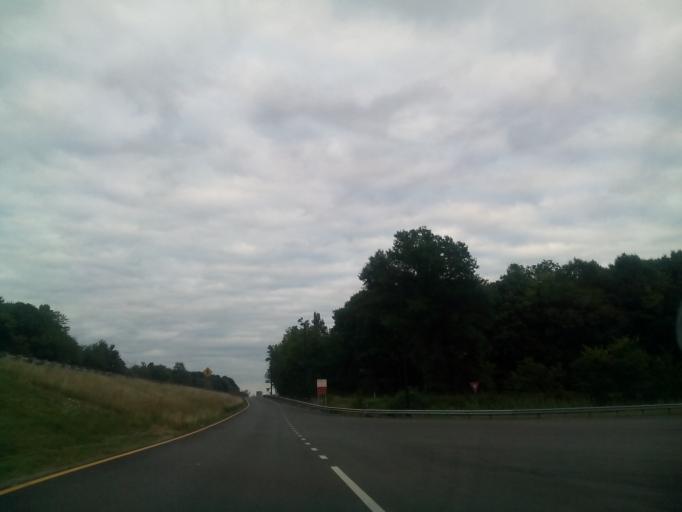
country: US
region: Ohio
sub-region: Portage County
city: Mantua
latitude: 41.2432
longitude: -81.1749
